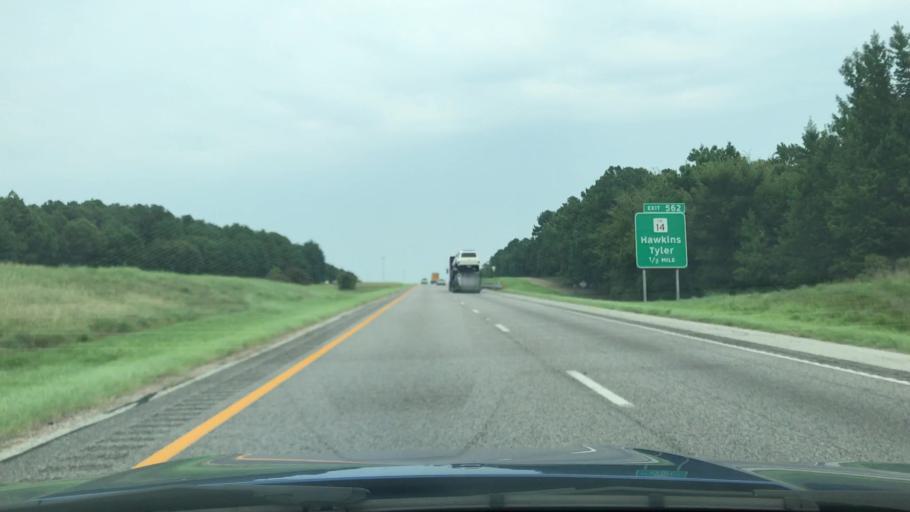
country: US
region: Texas
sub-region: Smith County
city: Tyler
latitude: 32.4554
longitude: -95.2995
